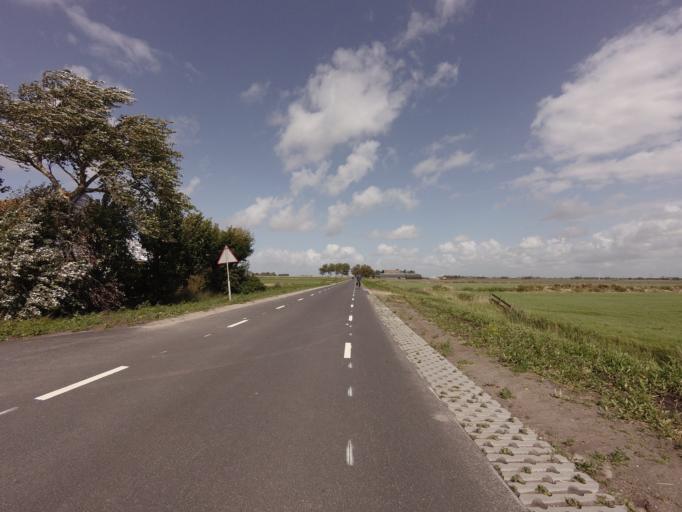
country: NL
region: Friesland
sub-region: Gemeente Harlingen
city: Harlingen
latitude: 53.1511
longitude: 5.4771
